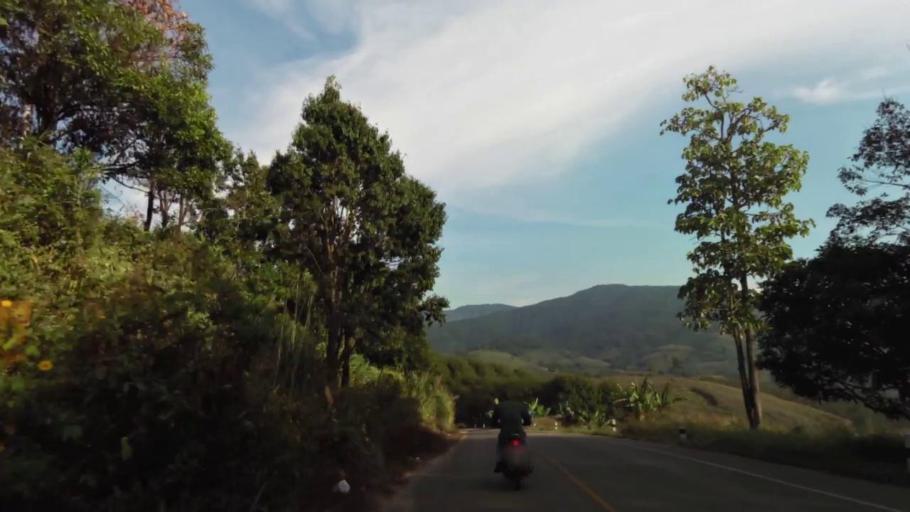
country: TH
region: Chiang Rai
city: Khun Tan
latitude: 19.8539
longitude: 100.3835
